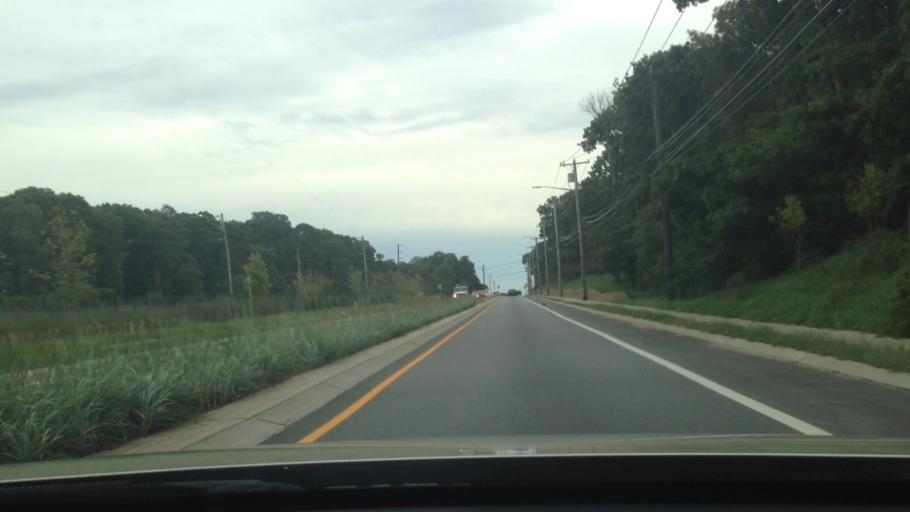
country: US
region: New York
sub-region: Suffolk County
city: Coram
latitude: 40.8529
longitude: -72.9979
